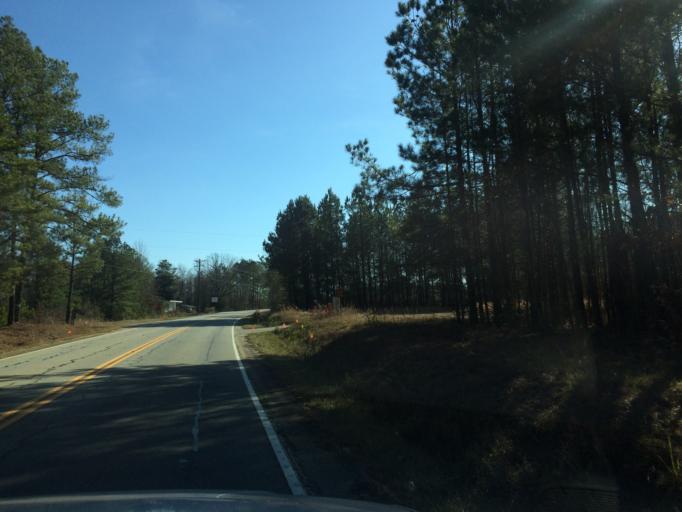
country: US
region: South Carolina
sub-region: Greenwood County
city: Ninety Six
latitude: 34.3153
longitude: -82.0499
